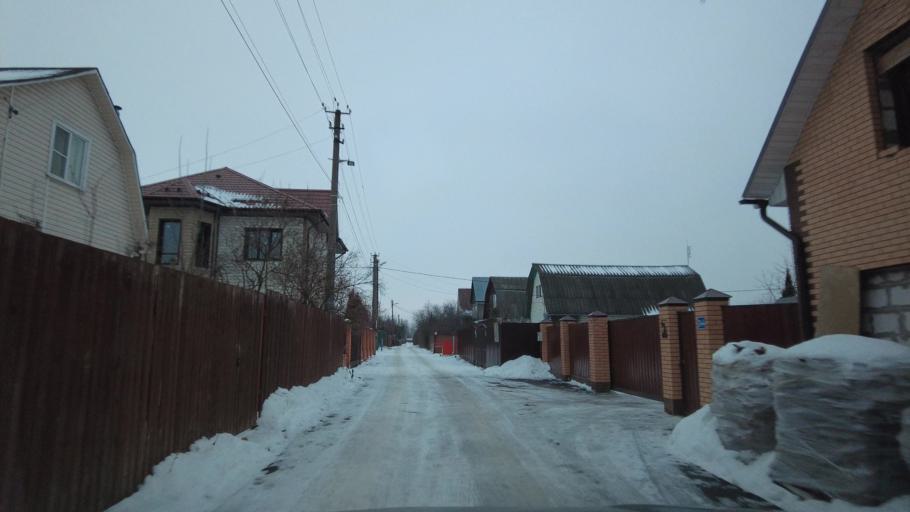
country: RU
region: Moskovskaya
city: Novopodrezkovo
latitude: 55.9838
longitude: 37.3921
